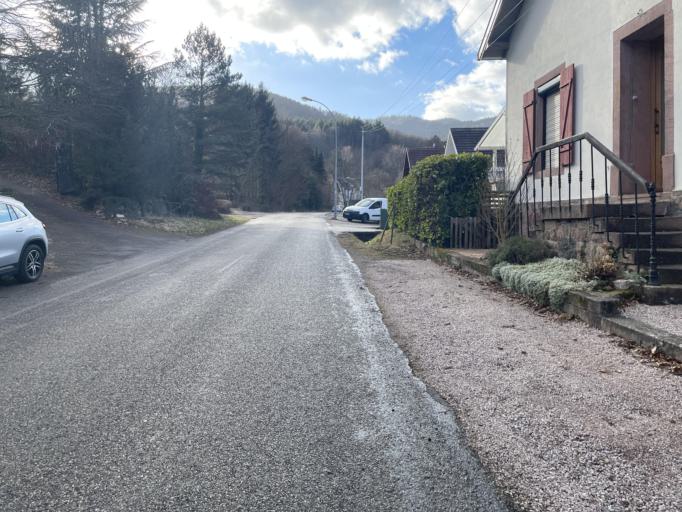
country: FR
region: Alsace
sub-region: Departement du Haut-Rhin
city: Buhl
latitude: 47.9220
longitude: 7.1784
